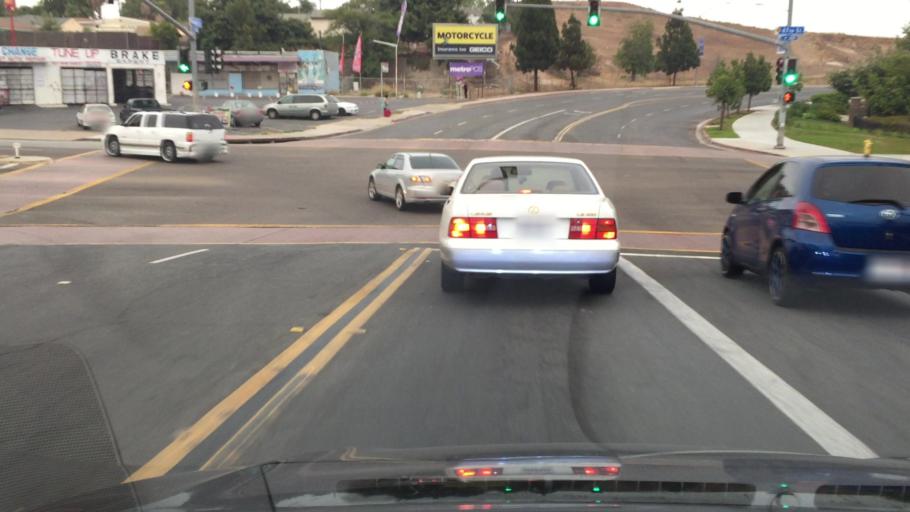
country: US
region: California
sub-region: San Diego County
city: National City
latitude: 32.7115
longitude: -117.0939
